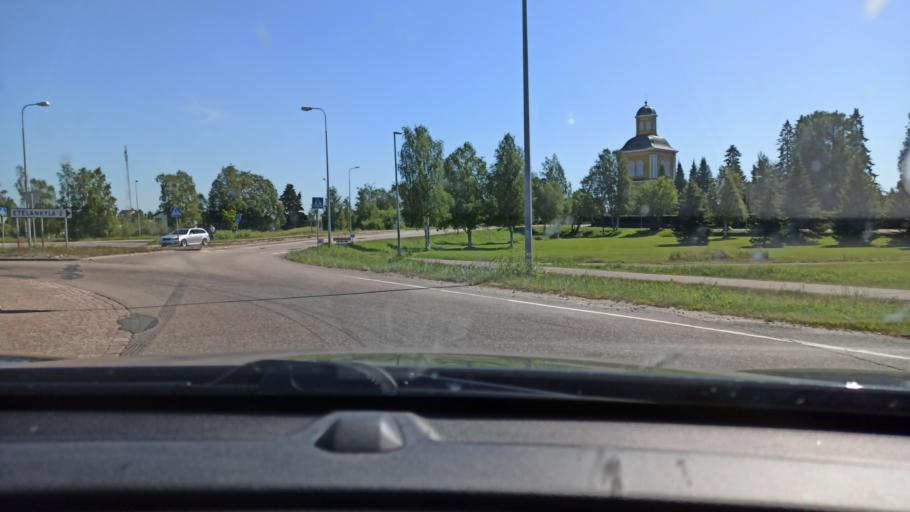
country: FI
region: Northern Ostrobothnia
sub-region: Ylivieska
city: Kalajoki
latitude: 64.2555
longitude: 23.9371
